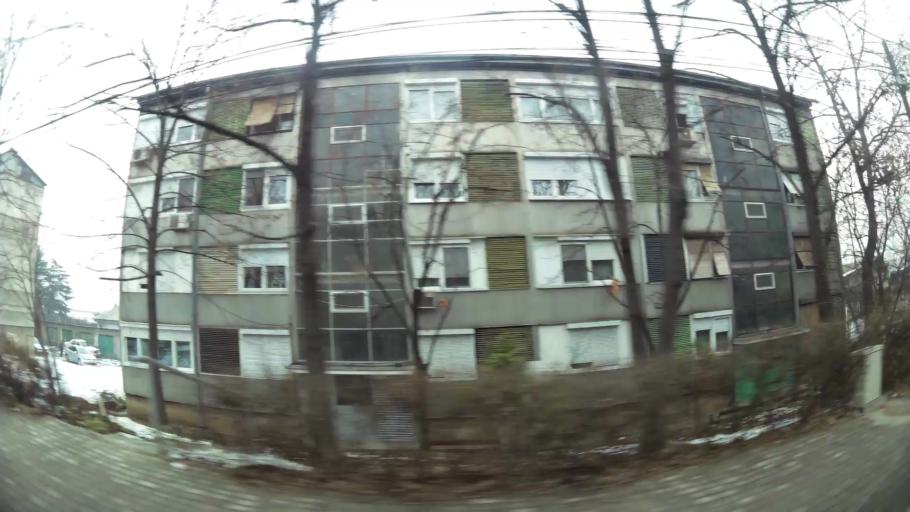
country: MK
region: Cair
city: Cair
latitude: 42.0119
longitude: 21.4589
